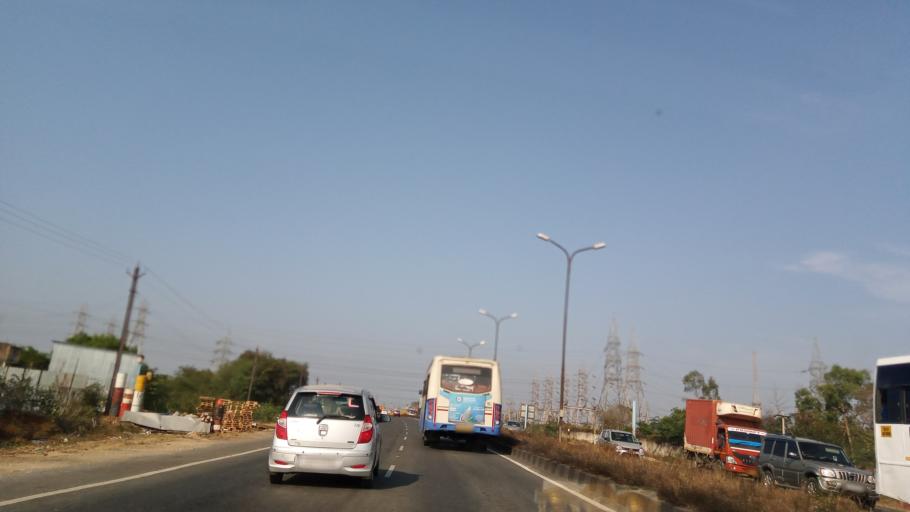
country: IN
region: Tamil Nadu
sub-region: Kancheepuram
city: Sriperumbudur
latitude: 12.9841
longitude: 79.9739
